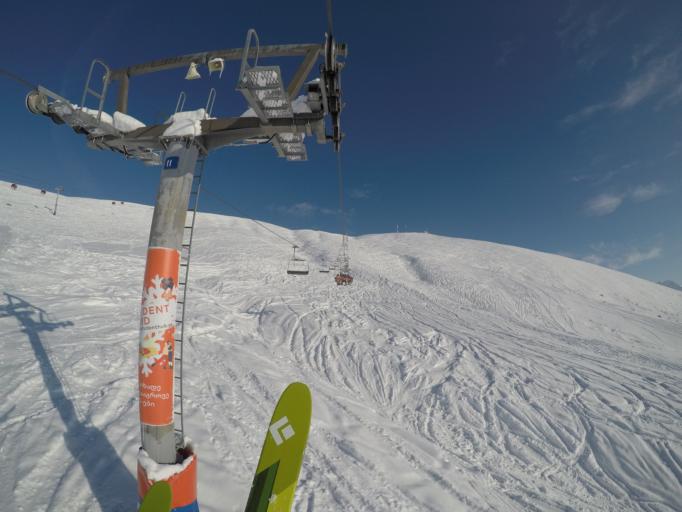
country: GE
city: Gudauri
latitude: 42.4827
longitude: 44.4947
